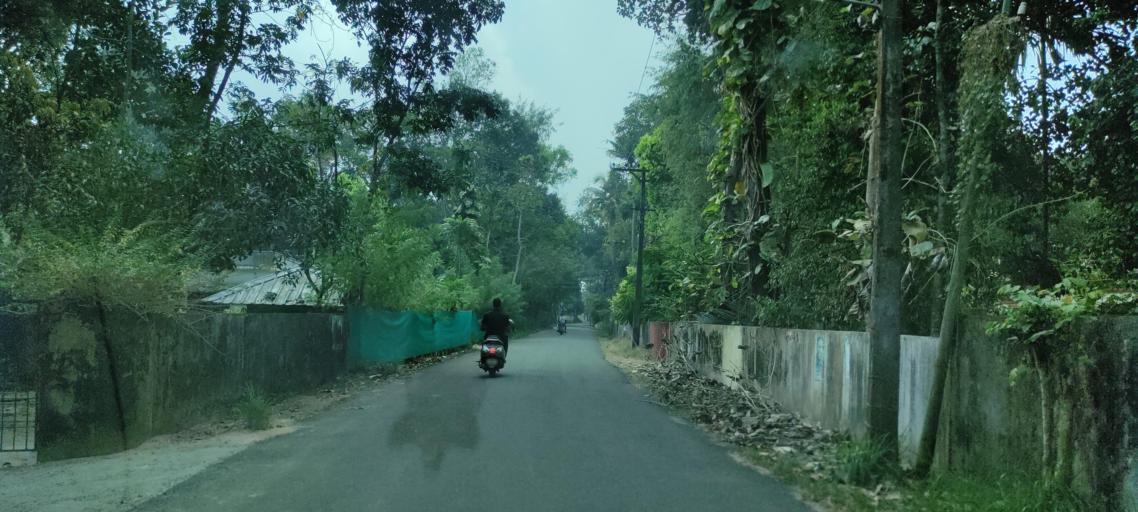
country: IN
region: Kerala
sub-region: Alappuzha
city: Shertallai
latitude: 9.6049
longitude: 76.3438
